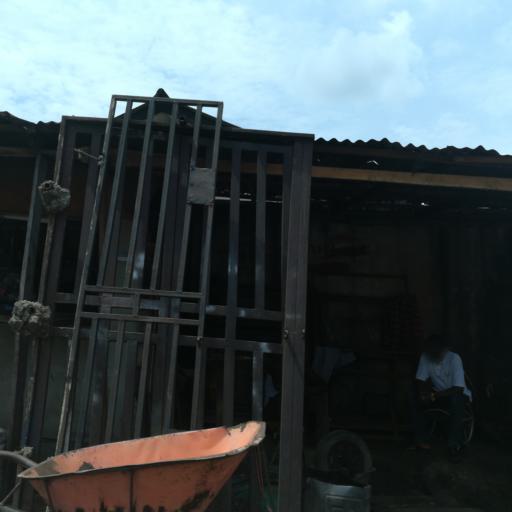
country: NG
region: Rivers
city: Port Harcourt
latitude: 4.7812
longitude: 7.0399
